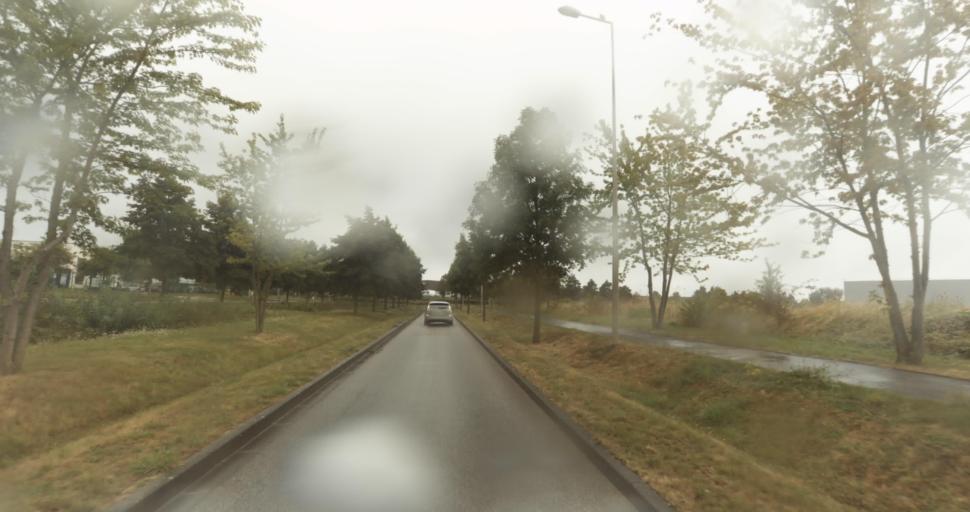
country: FR
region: Haute-Normandie
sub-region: Departement de l'Eure
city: Evreux
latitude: 49.0098
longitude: 1.1804
